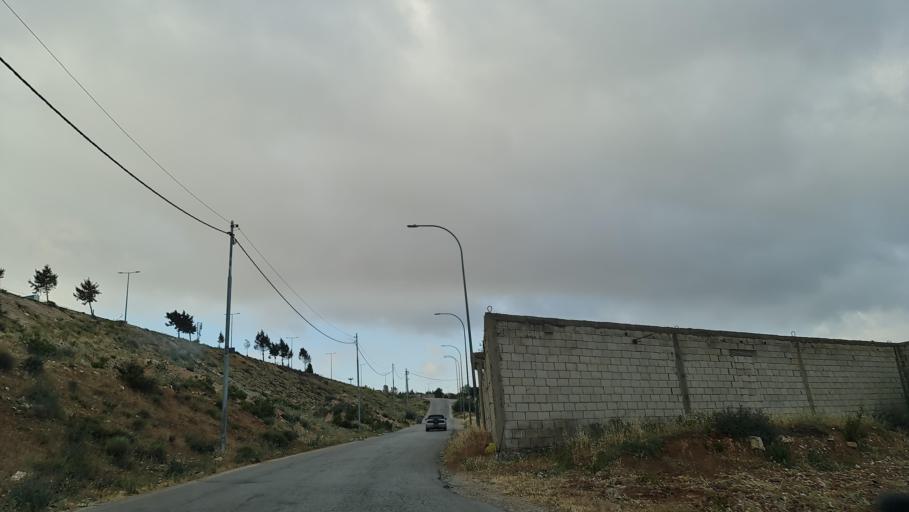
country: JO
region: Amman
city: Al Jubayhah
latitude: 32.0911
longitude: 35.8948
